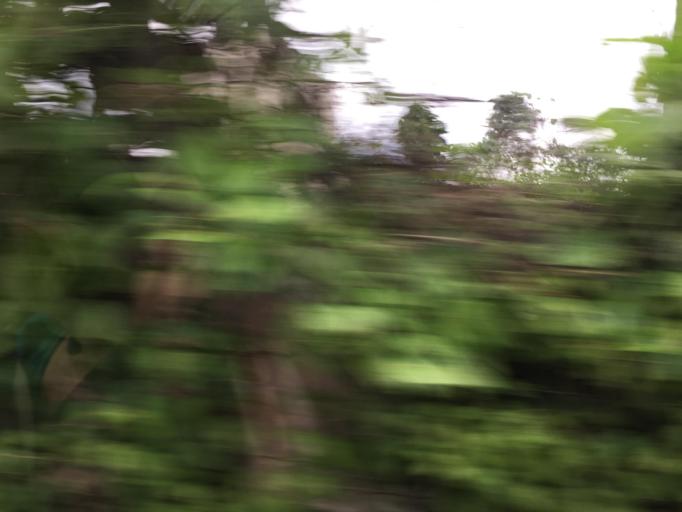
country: GT
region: Sacatepequez
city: Antigua Guatemala
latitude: 14.5515
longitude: -90.7464
